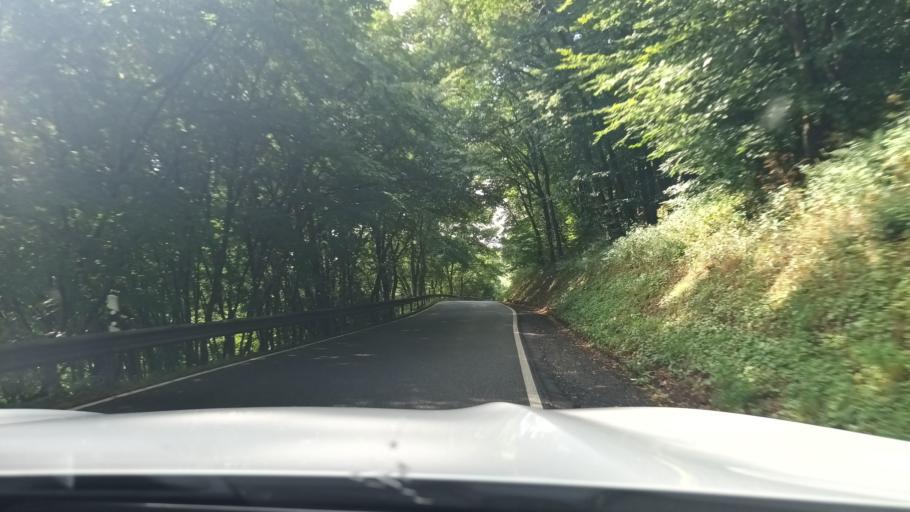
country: DE
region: North Rhine-Westphalia
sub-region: Regierungsbezirk Koln
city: Hennef
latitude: 50.7417
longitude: 7.3136
